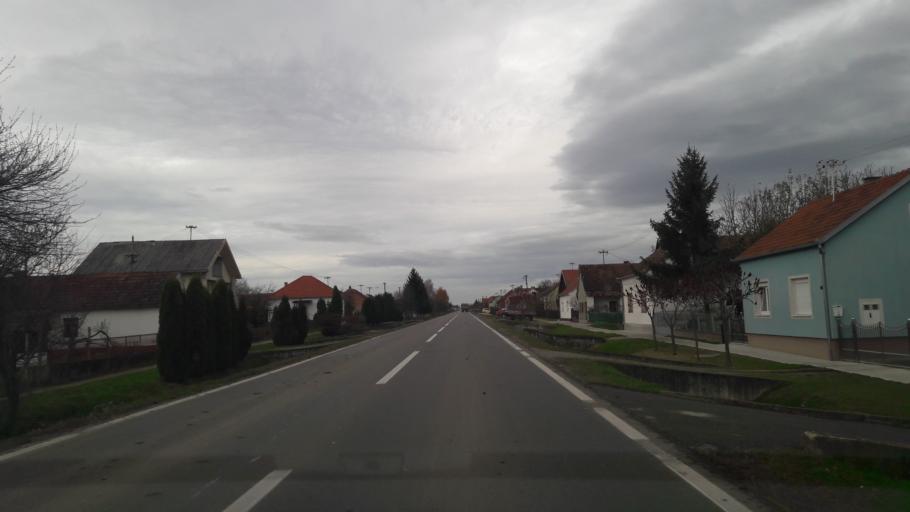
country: HR
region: Osjecko-Baranjska
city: Fericanci
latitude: 45.5276
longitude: 17.9584
